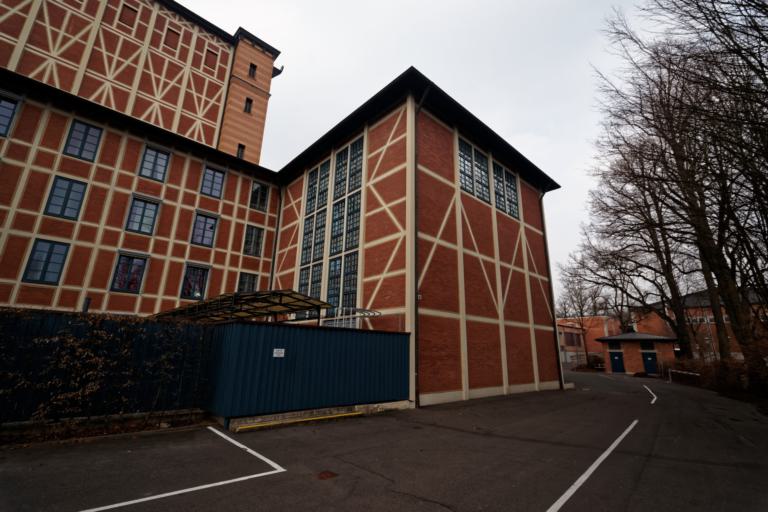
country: DE
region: Bavaria
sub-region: Upper Franconia
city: Bayreuth
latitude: 49.9598
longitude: 11.5803
